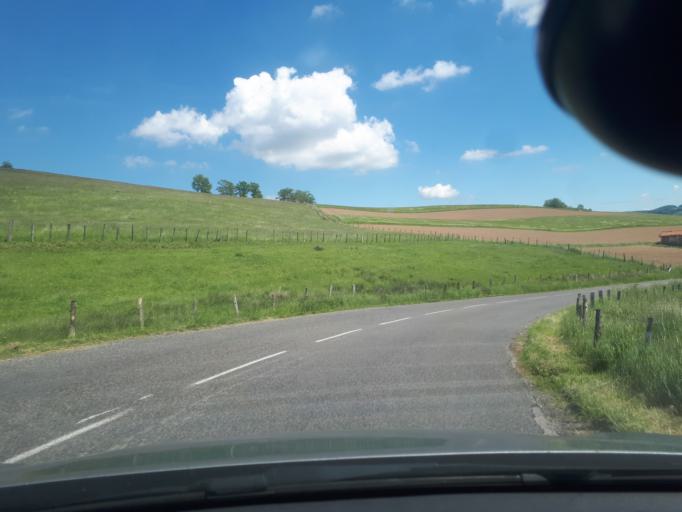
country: FR
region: Rhone-Alpes
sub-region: Departement du Rhone
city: Saint-Martin-en-Haut
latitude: 45.6802
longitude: 4.5448
